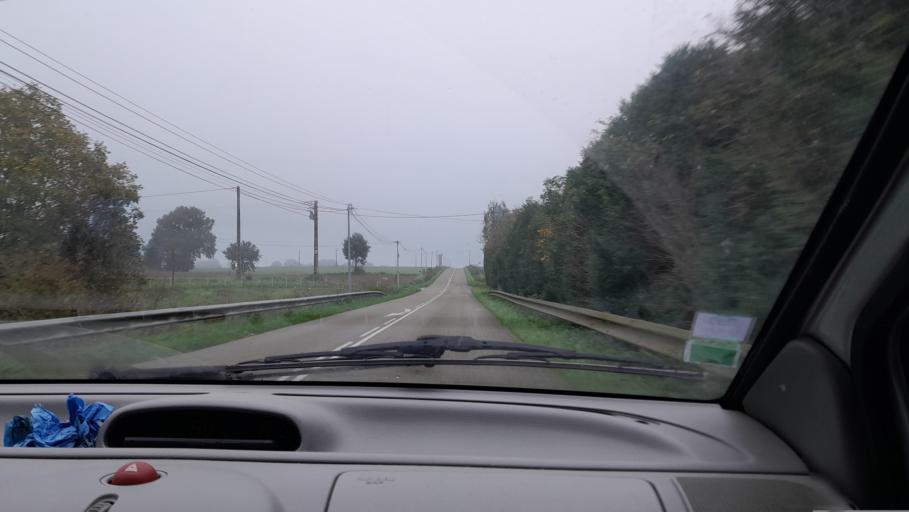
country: FR
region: Brittany
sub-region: Departement d'Ille-et-Vilaine
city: Le Pertre
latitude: 47.9954
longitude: -0.9817
